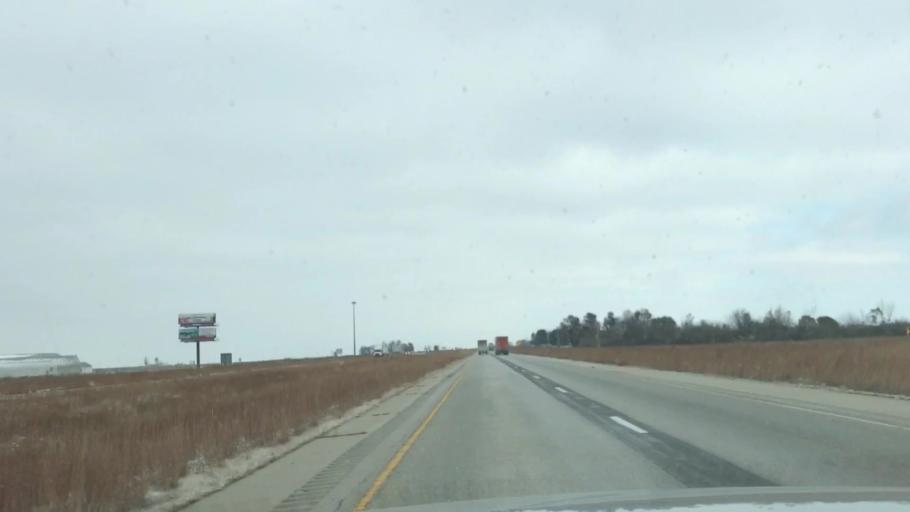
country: US
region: Illinois
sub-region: Sangamon County
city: Divernon
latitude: 39.4463
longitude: -89.6439
